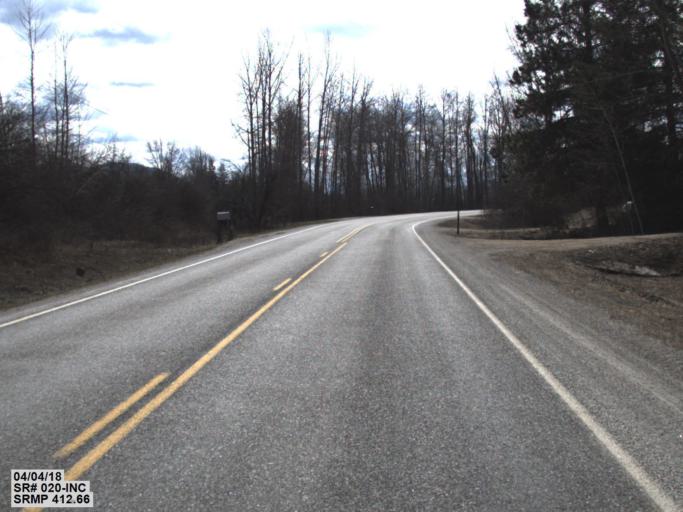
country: US
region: Washington
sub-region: Pend Oreille County
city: Newport
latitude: 48.4265
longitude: -117.3172
